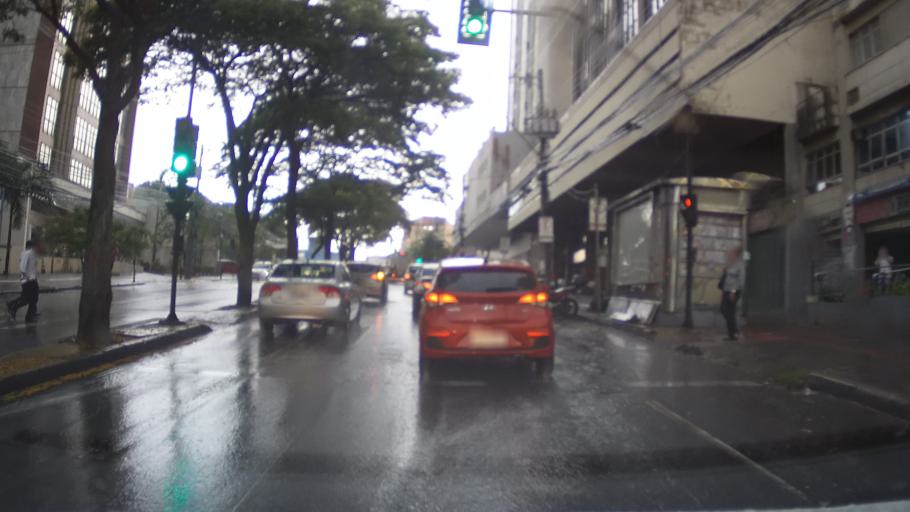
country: BR
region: Minas Gerais
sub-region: Belo Horizonte
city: Belo Horizonte
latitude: -19.9485
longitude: -43.9610
